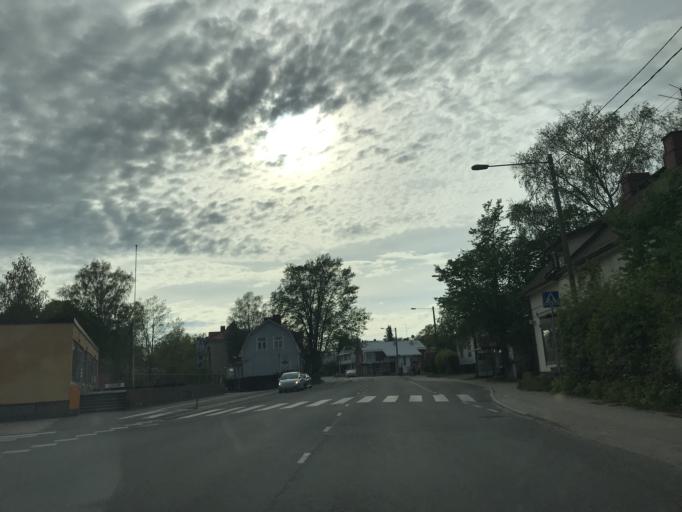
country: FI
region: Varsinais-Suomi
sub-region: Turku
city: Turku
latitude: 60.4557
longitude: 22.3063
